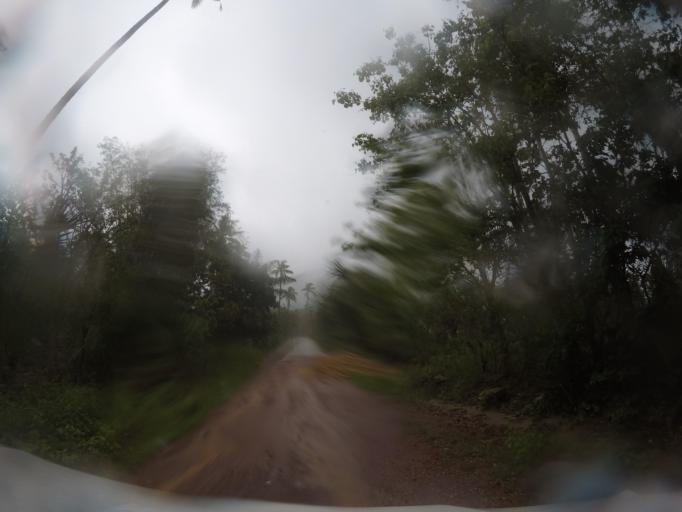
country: TL
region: Baucau
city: Venilale
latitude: -8.6298
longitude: 126.4426
